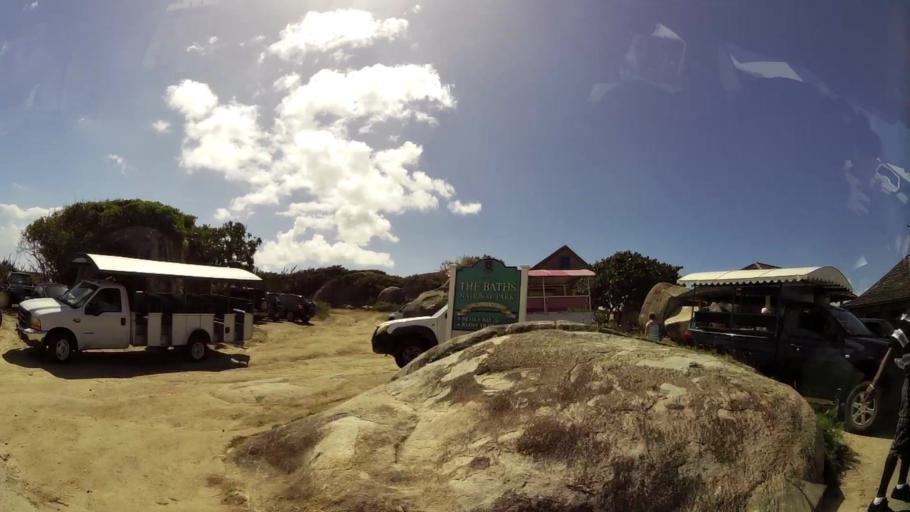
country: VG
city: Tortola
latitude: 18.4291
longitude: -64.4422
